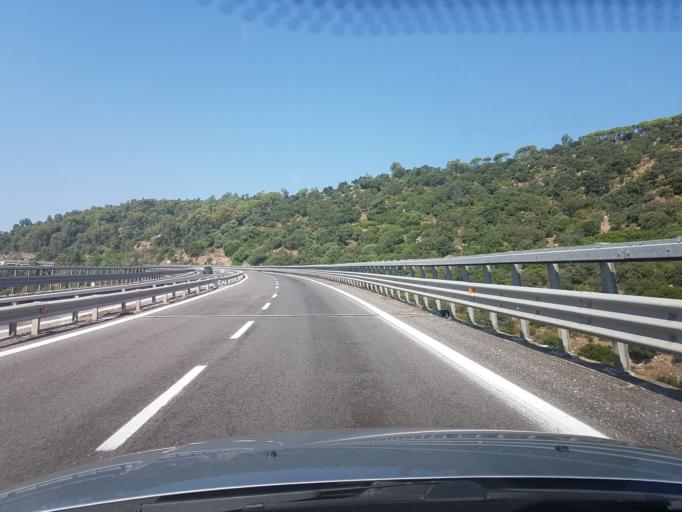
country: IT
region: Sardinia
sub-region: Provincia di Nuoro
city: Nuoro
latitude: 40.3398
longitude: 9.3057
